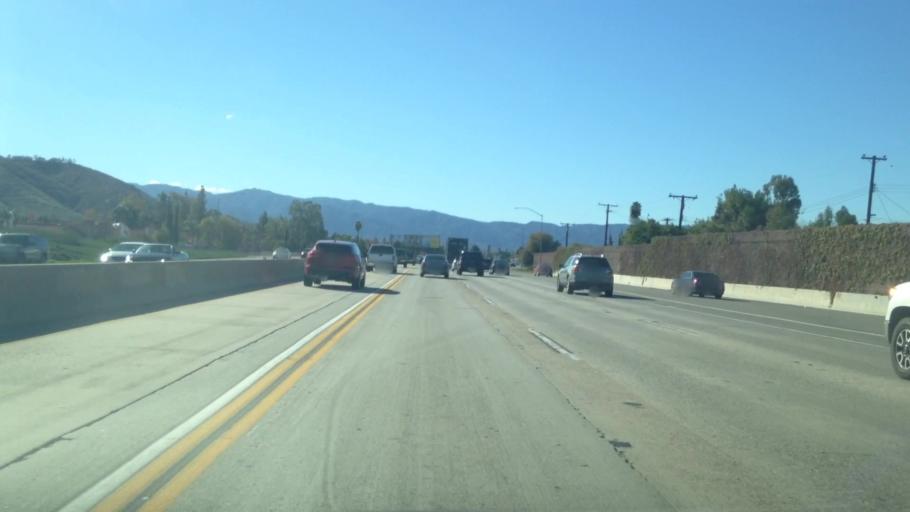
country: US
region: California
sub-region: Riverside County
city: Home Gardens
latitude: 33.8984
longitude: -117.4749
